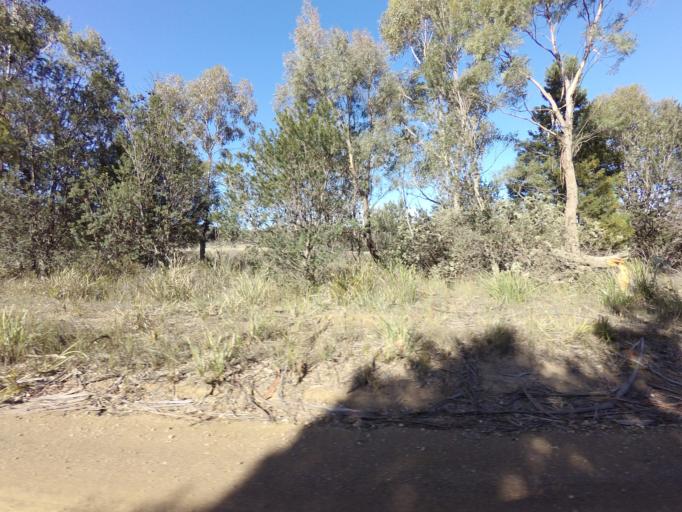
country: AU
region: Tasmania
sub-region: Sorell
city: Sorell
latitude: -42.3526
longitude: 147.9686
